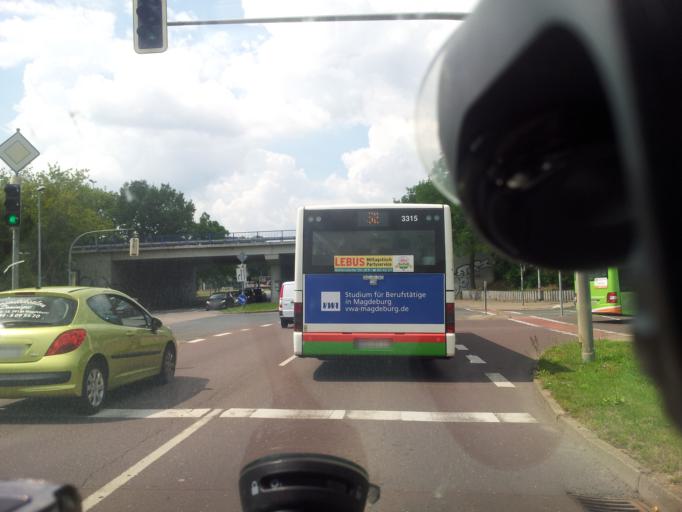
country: DE
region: Saxony-Anhalt
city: Magdeburg
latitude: 52.1116
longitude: 11.6108
